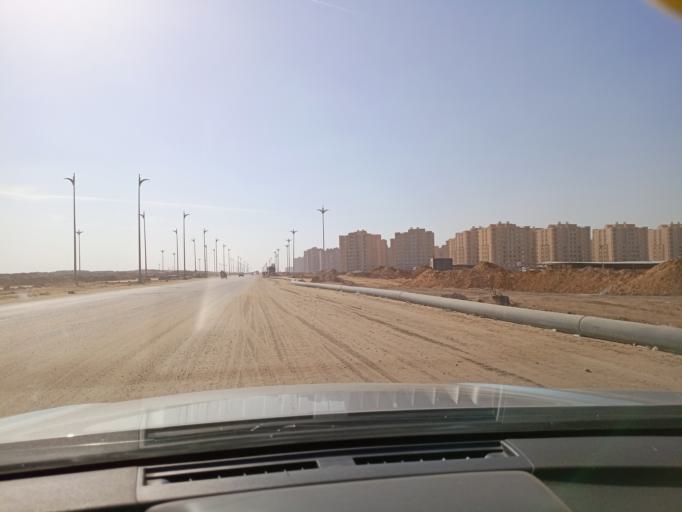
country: EG
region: Muhafazat al Qalyubiyah
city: Al Khankah
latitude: 30.0231
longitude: 31.6651
